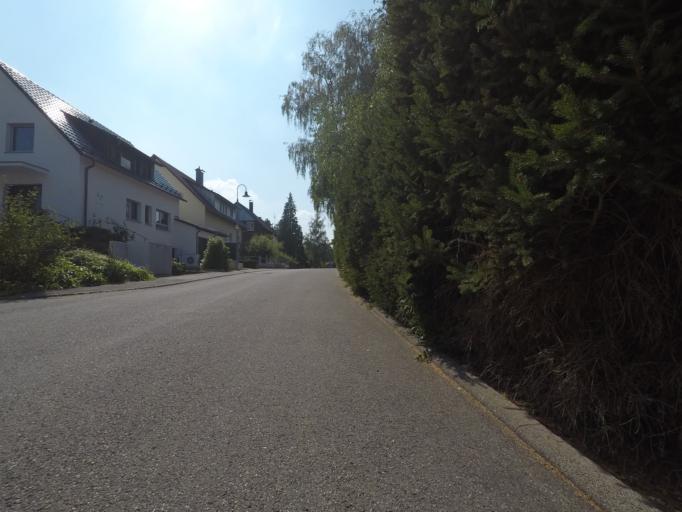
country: DE
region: Baden-Wuerttemberg
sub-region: Regierungsbezirk Stuttgart
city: Steinenbronn
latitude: 48.6559
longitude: 9.1152
